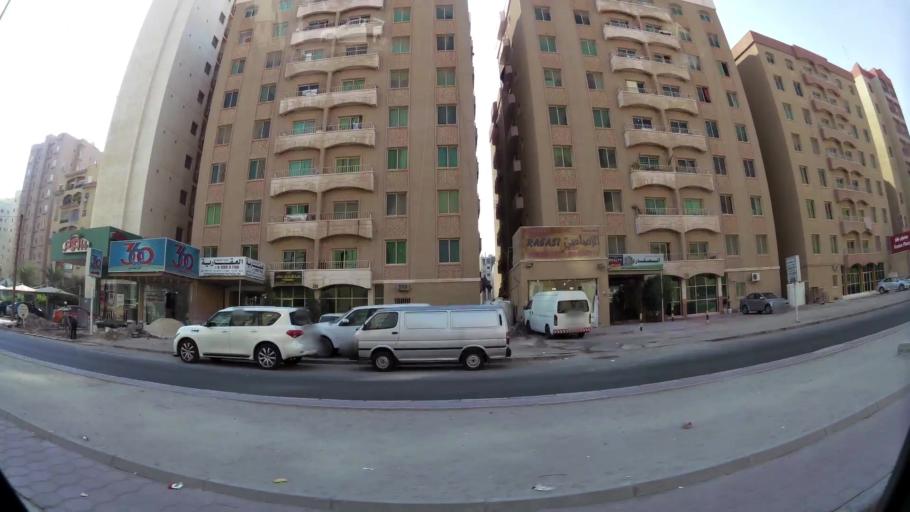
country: KW
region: Al Ahmadi
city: Al Mahbulah
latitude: 29.1470
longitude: 48.1207
